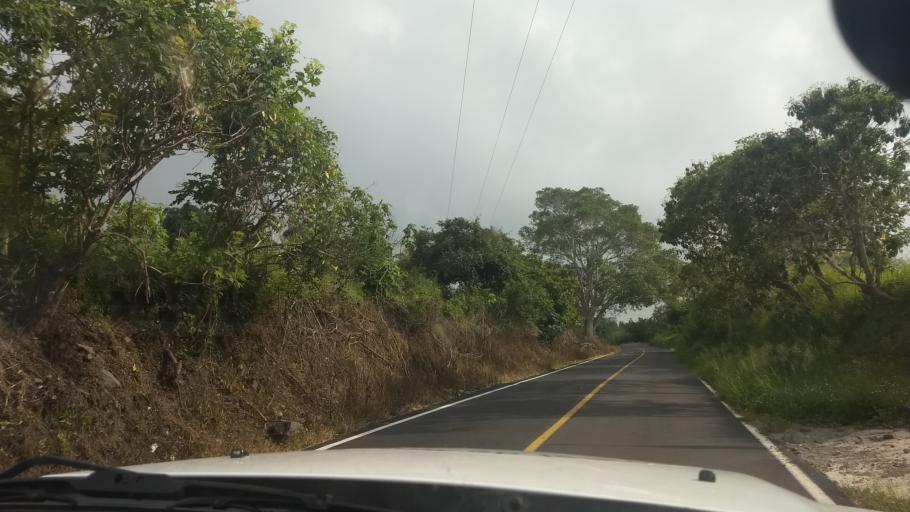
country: MX
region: Colima
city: Queseria
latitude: 19.4026
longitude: -103.6169
